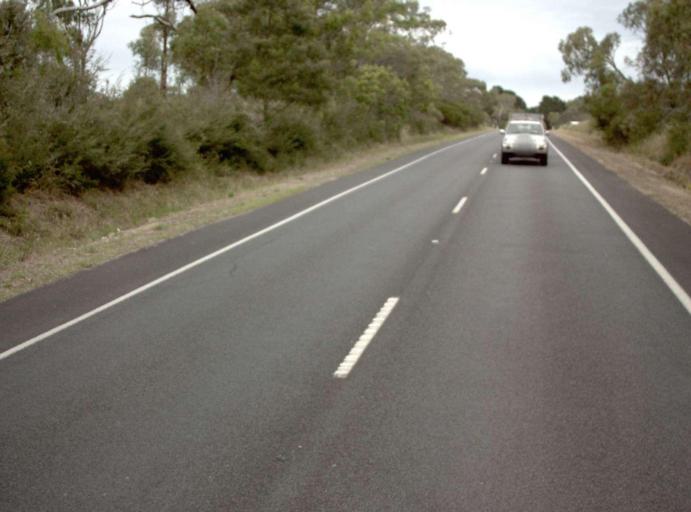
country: AU
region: Victoria
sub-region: Wellington
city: Sale
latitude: -38.1791
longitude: 147.0849
